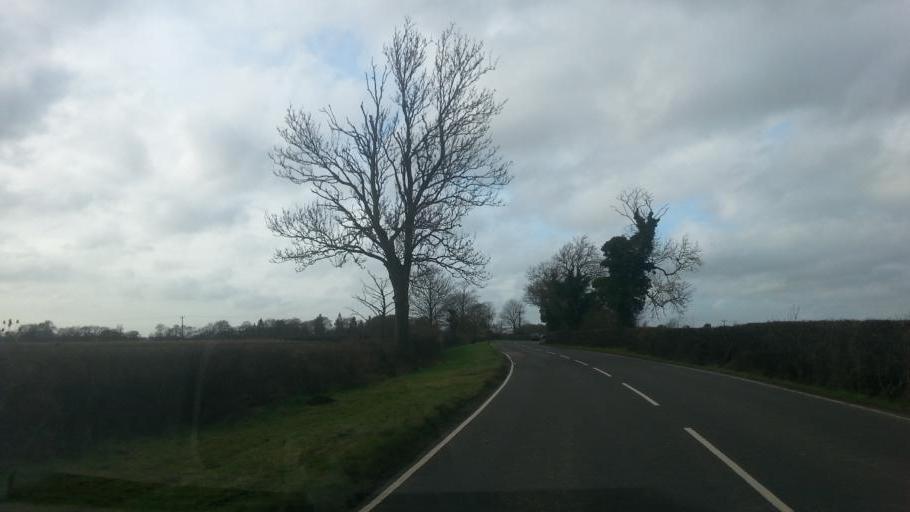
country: GB
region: England
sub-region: District of Rutland
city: Edith Weston
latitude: 52.6360
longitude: -0.6547
